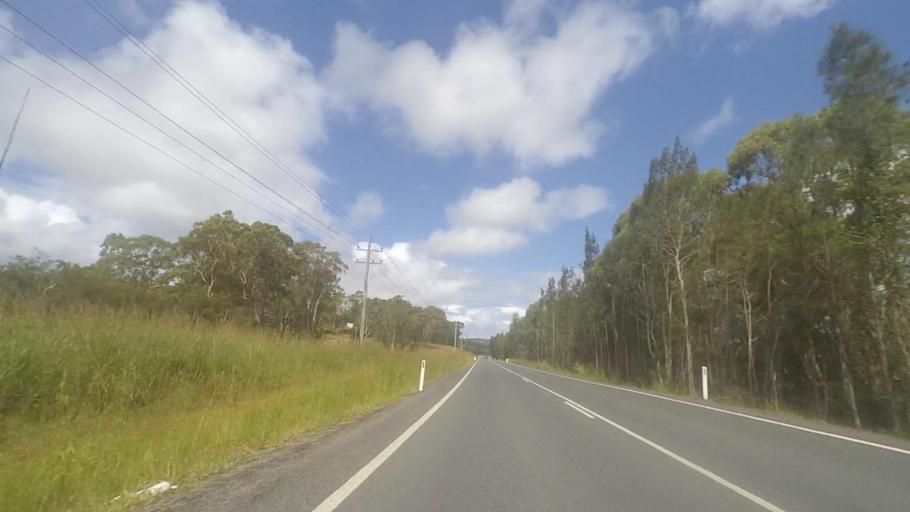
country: AU
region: New South Wales
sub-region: Great Lakes
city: Bulahdelah
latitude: -32.3848
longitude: 152.3995
